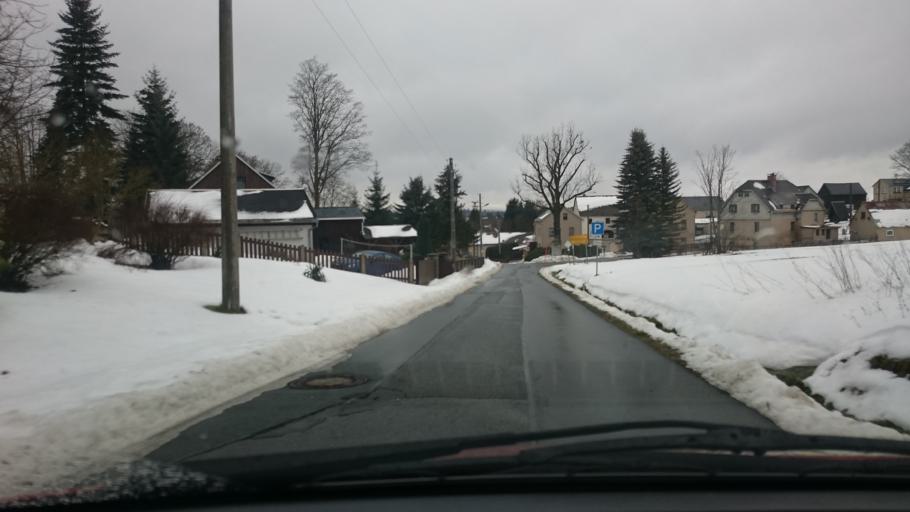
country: DE
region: Saxony
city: Markneukirchen
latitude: 50.2709
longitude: 12.3300
